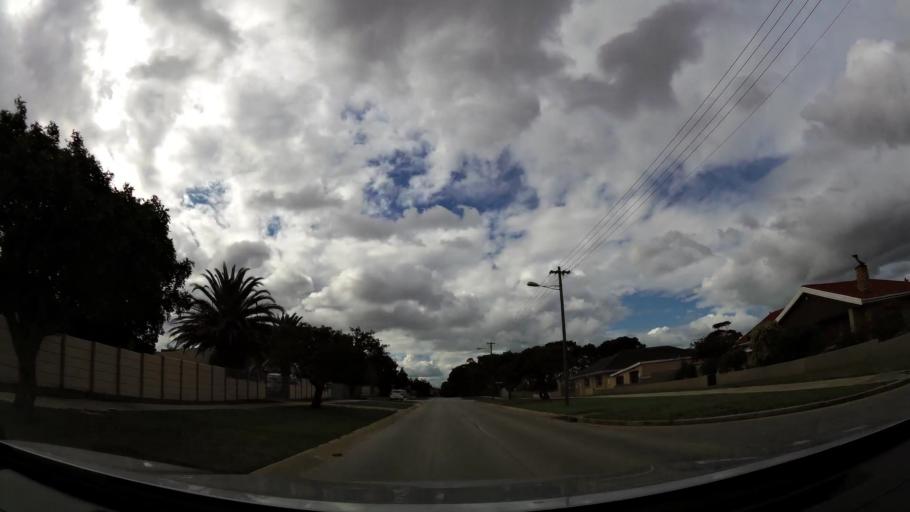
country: ZA
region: Eastern Cape
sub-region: Nelson Mandela Bay Metropolitan Municipality
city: Port Elizabeth
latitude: -33.9347
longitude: 25.5254
